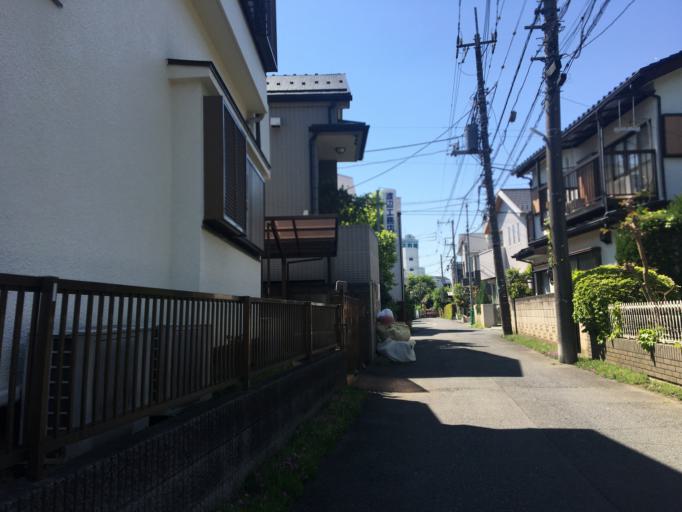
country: JP
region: Tokyo
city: Higashimurayama-shi
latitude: 35.7404
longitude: 139.4875
